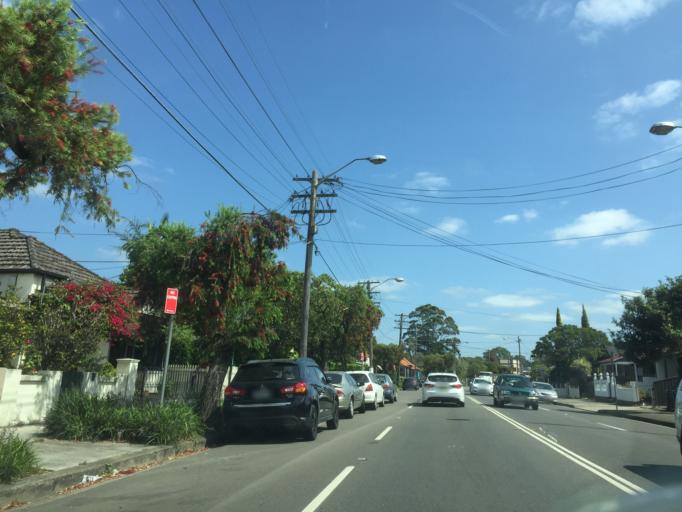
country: AU
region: New South Wales
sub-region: Marrickville
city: Marrickville
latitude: -33.9089
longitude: 151.1608
